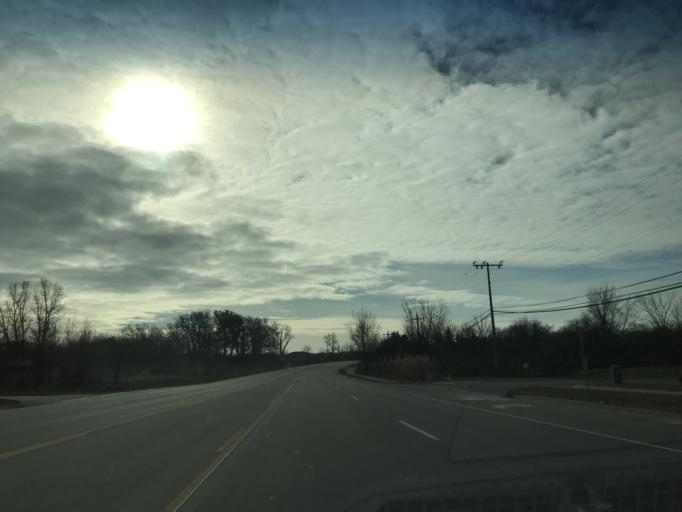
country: US
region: Michigan
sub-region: Oakland County
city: Auburn Hills
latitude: 42.6755
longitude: -83.2524
